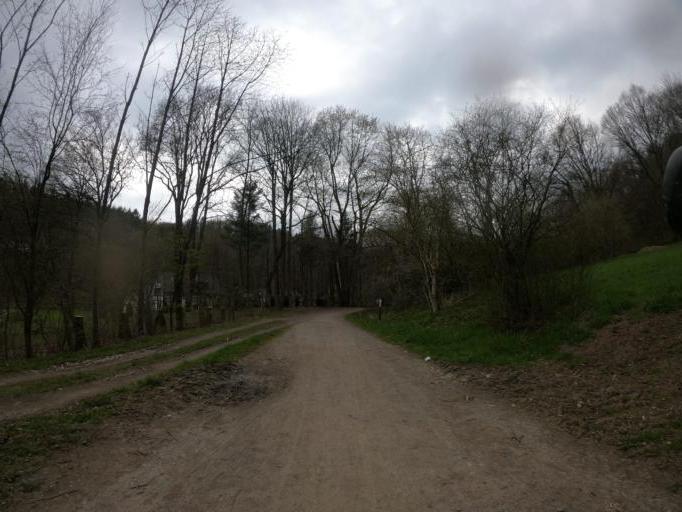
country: DE
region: North Rhine-Westphalia
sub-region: Regierungsbezirk Koln
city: Hurtgenwald
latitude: 50.6858
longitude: 6.4116
